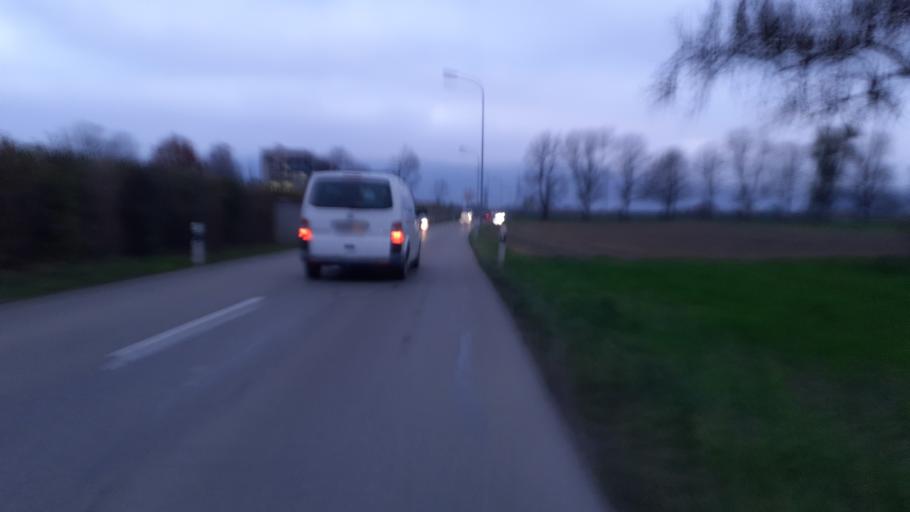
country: AT
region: Vorarlberg
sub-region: Politischer Bezirk Feldkirch
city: Mader
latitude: 47.3597
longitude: 9.6037
